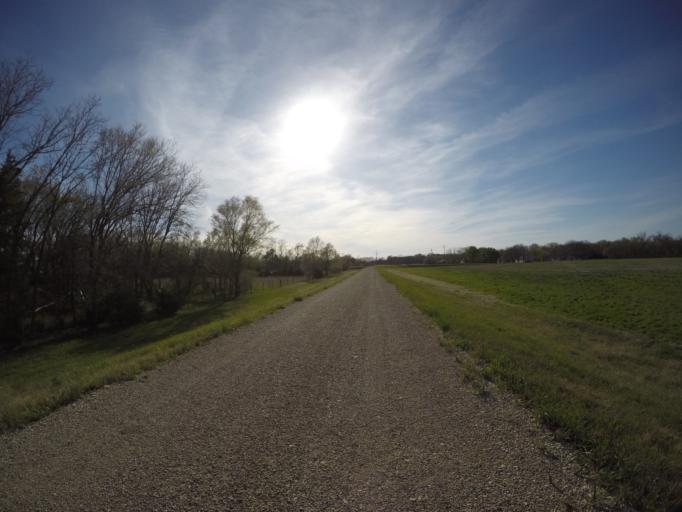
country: US
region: Kansas
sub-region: Saline County
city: Salina
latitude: 38.8649
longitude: -97.6054
